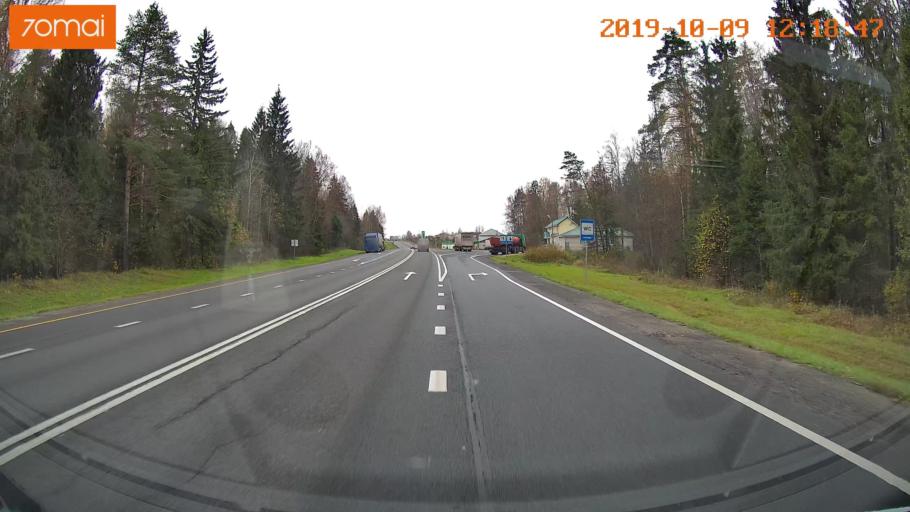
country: RU
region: Jaroslavl
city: Prechistoye
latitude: 58.4375
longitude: 40.3214
